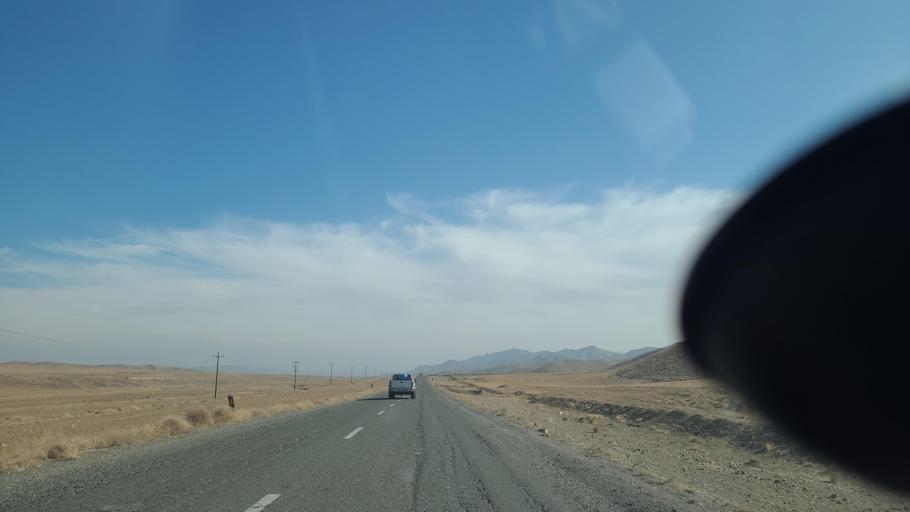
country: IR
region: Razavi Khorasan
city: Fariman
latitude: 35.5903
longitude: 59.6159
